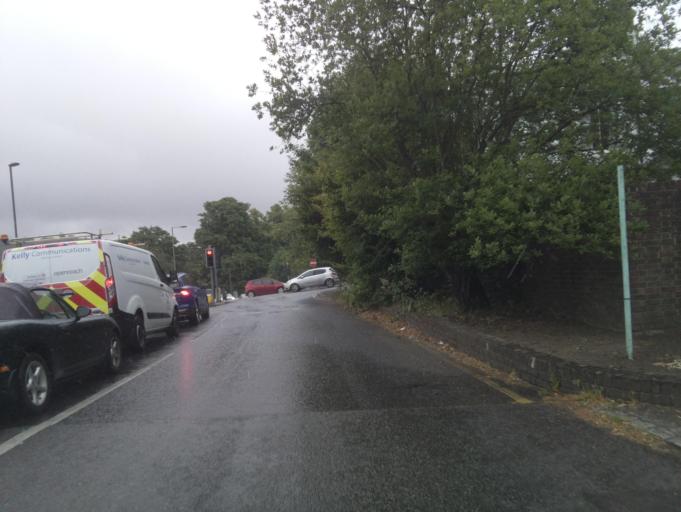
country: GB
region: England
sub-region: Surrey
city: Redhill
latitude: 51.2326
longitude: -0.1729
